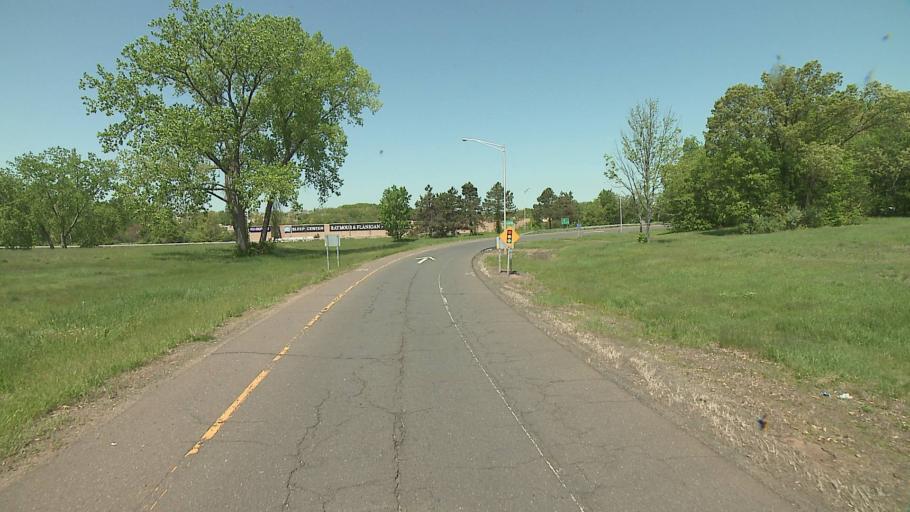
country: US
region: Connecticut
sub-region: Hartford County
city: Manchester
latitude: 41.8115
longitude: -72.5239
